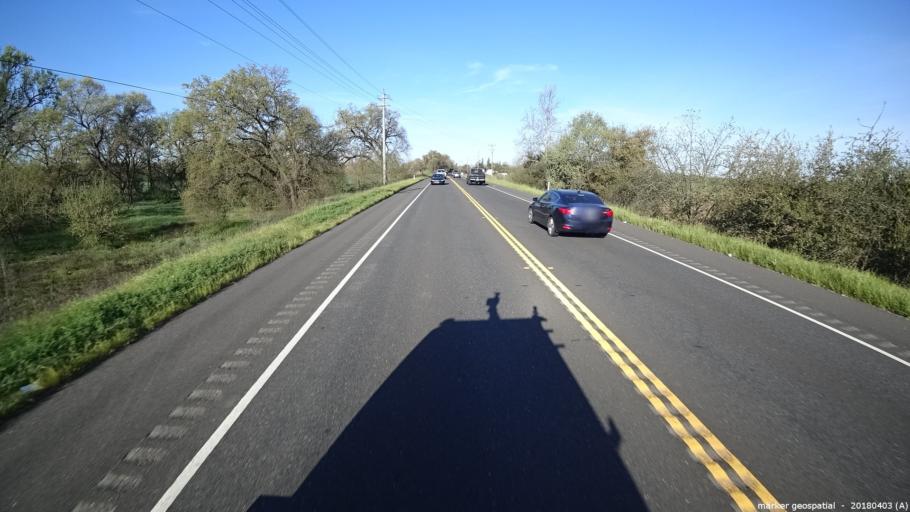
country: US
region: California
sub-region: Sacramento County
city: Rancho Murieta
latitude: 38.4929
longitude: -121.1657
